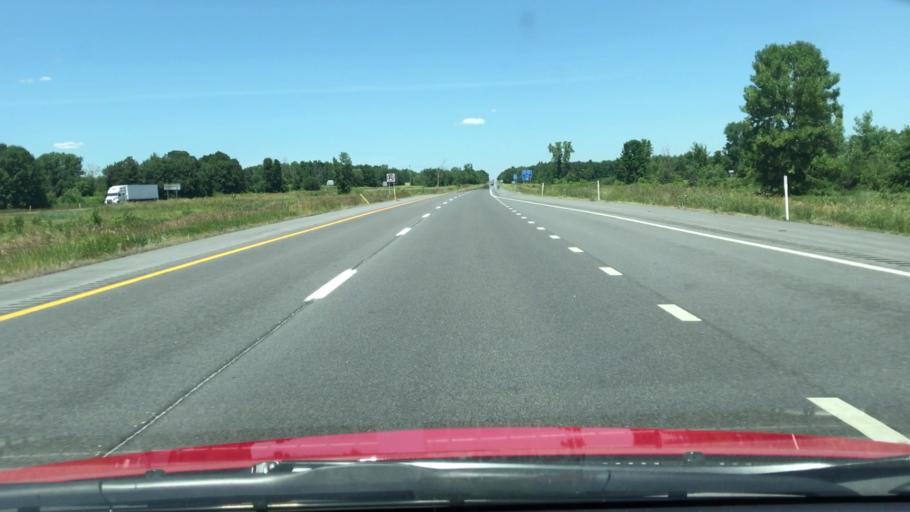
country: US
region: New York
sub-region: Clinton County
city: Cumberland Head
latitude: 44.7853
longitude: -73.4385
